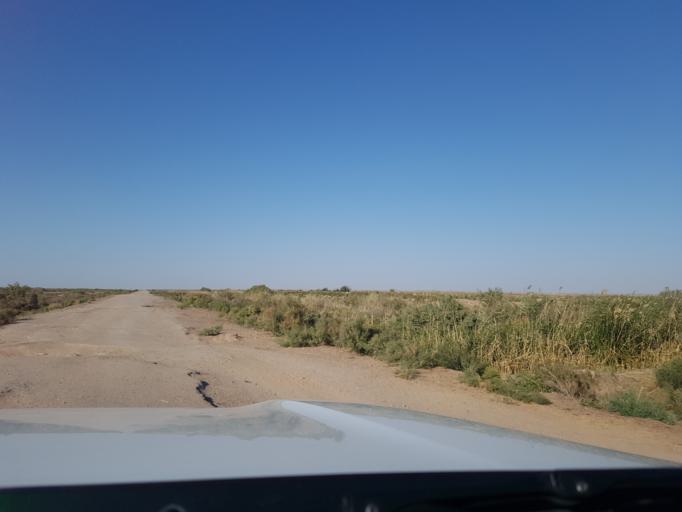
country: IR
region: Razavi Khorasan
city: Sarakhs
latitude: 36.9617
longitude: 61.3823
